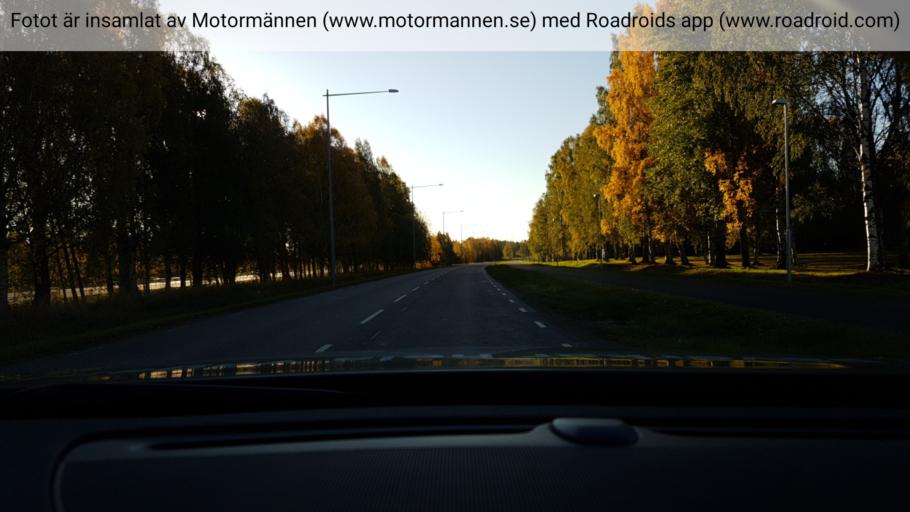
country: SE
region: Norrbotten
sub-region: Lulea Kommun
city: Gammelstad
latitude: 65.6397
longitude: 22.0215
